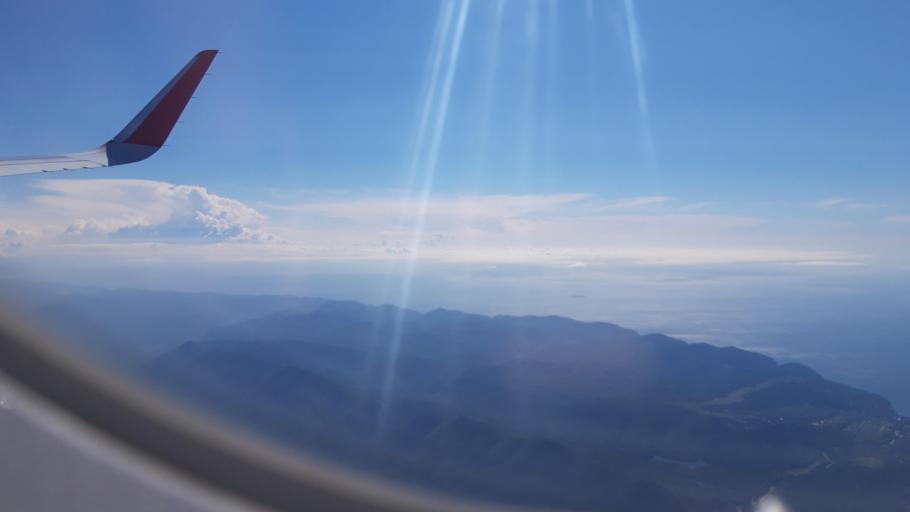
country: RU
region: Krasnodarskiy
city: Gelendzhik
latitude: 44.6120
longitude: 38.1650
